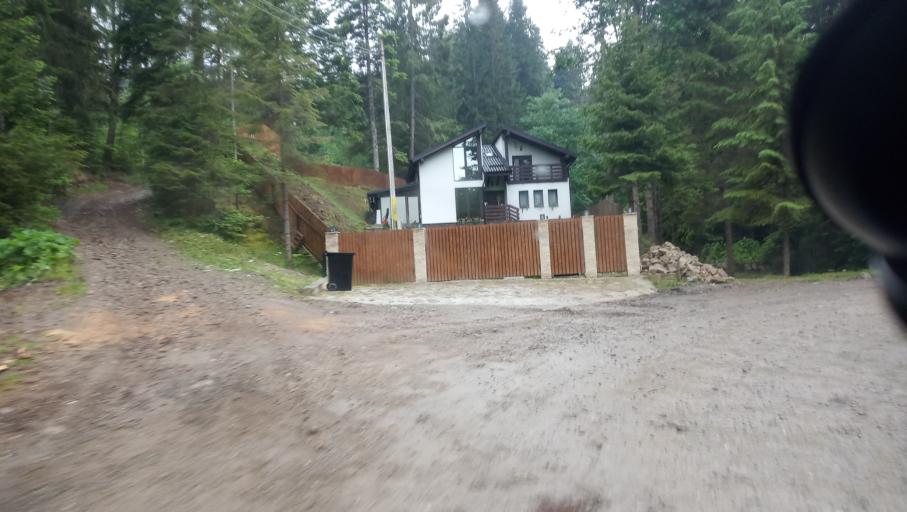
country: RO
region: Neamt
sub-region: Comuna Ceahlau
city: Ceahlau
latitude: 46.9935
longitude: 25.9216
